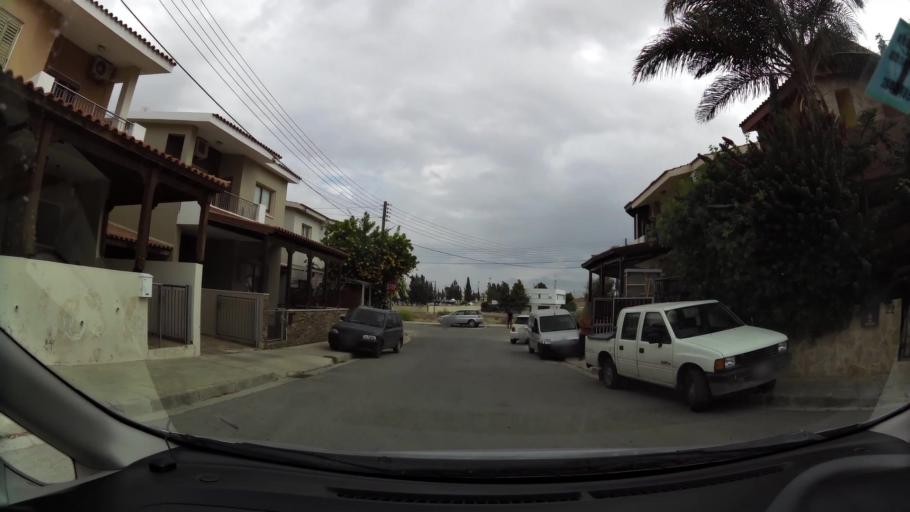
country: CY
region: Lefkosia
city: Geri
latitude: 35.1162
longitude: 33.3867
